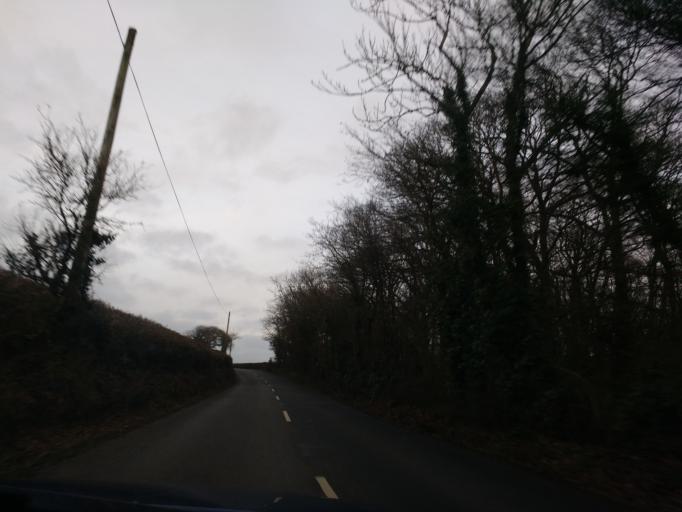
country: GB
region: England
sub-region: Isle of Wight
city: Northwood
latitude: 50.7341
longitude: -1.3422
